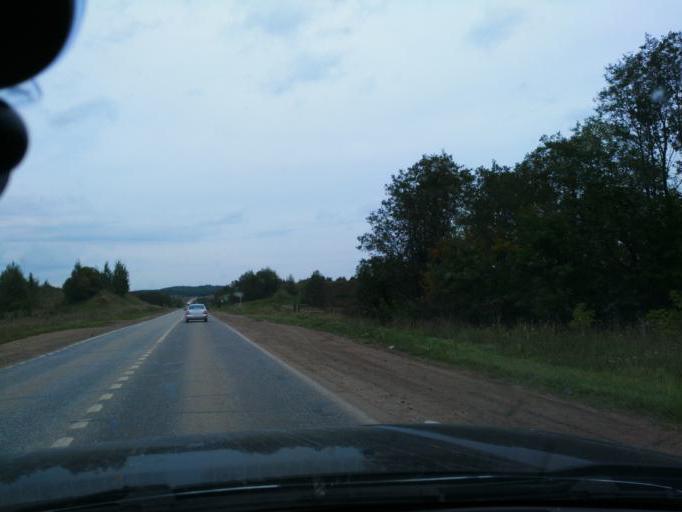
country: RU
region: Perm
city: Chernushka
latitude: 56.5547
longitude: 56.1103
